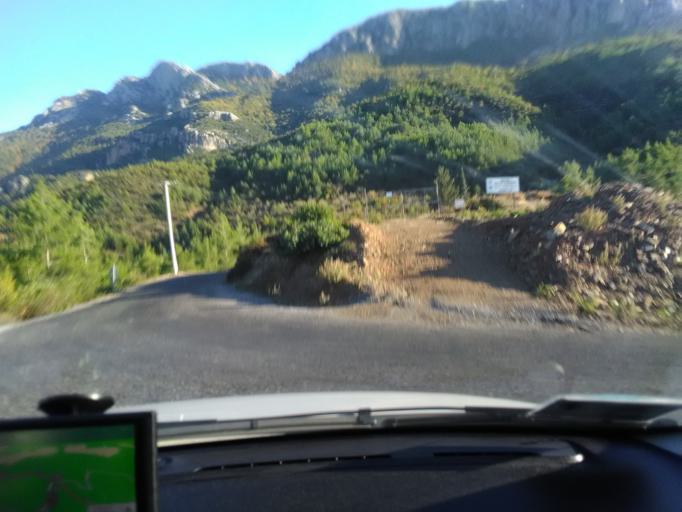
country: TR
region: Antalya
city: Gazipasa
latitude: 36.3061
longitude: 32.3988
